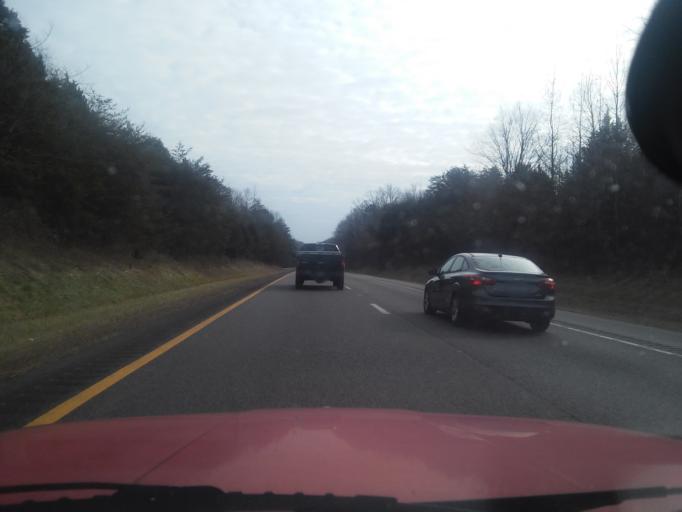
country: US
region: Virginia
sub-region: Goochland County
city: Goochland
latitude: 37.8175
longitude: -77.9465
